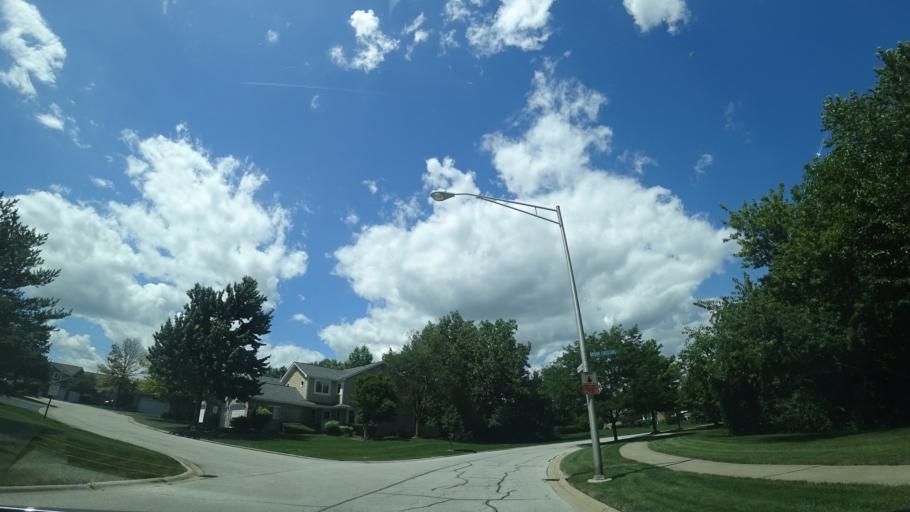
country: US
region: Illinois
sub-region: Will County
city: Mokena
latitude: 41.5735
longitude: -87.8944
